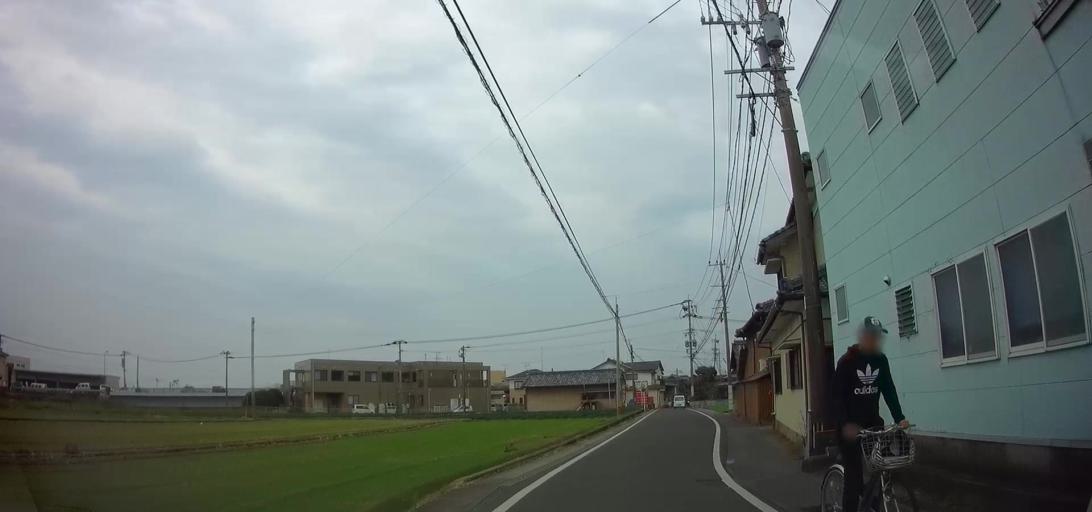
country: JP
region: Nagasaki
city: Shimabara
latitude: 32.6617
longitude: 130.2997
